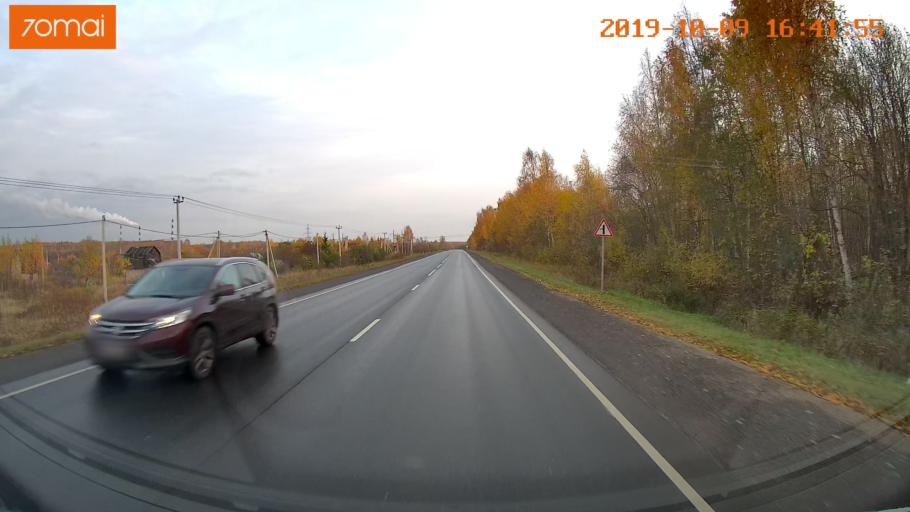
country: RU
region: Kostroma
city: Volgorechensk
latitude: 57.4679
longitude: 41.0902
